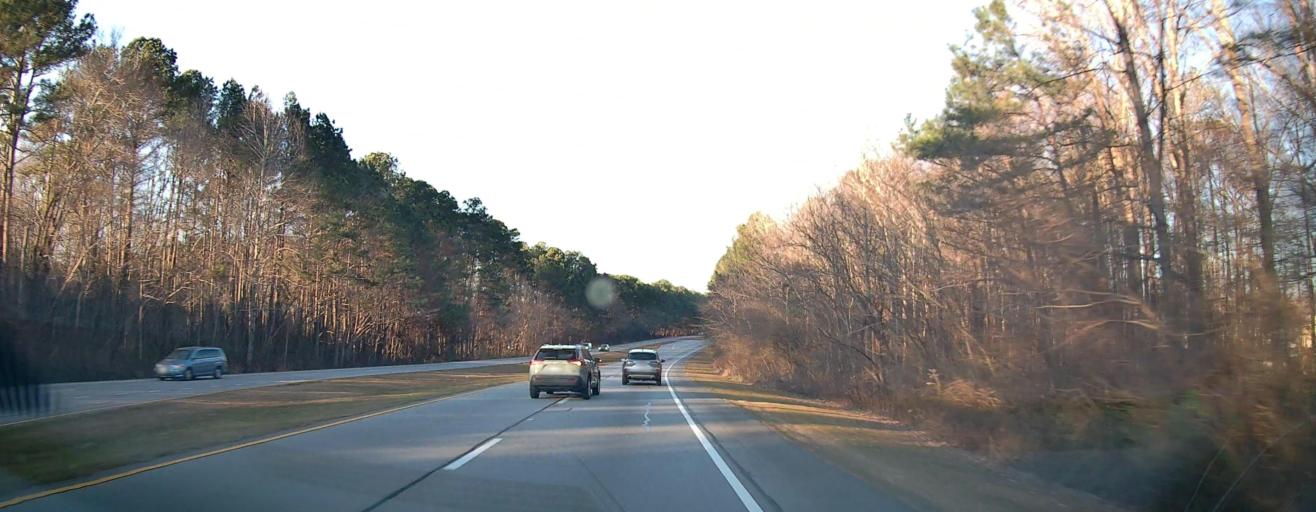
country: US
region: Georgia
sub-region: Fayette County
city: Peachtree City
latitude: 33.4253
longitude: -84.6033
